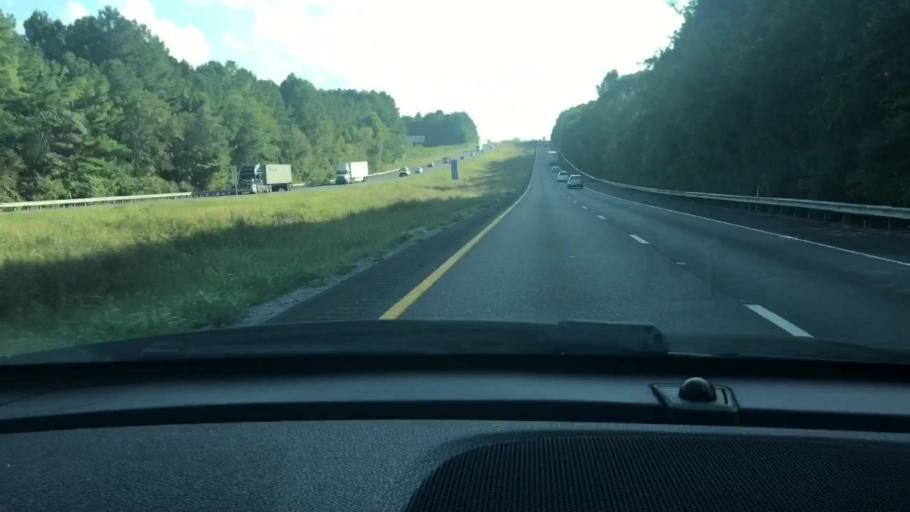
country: US
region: Tennessee
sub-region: Sumner County
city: Millersville
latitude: 36.4300
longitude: -86.7109
